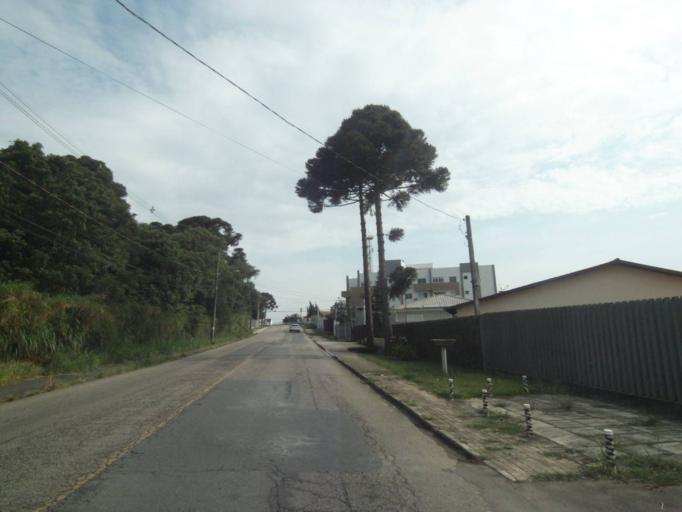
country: BR
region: Parana
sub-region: Curitiba
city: Curitiba
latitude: -25.4060
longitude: -49.3136
